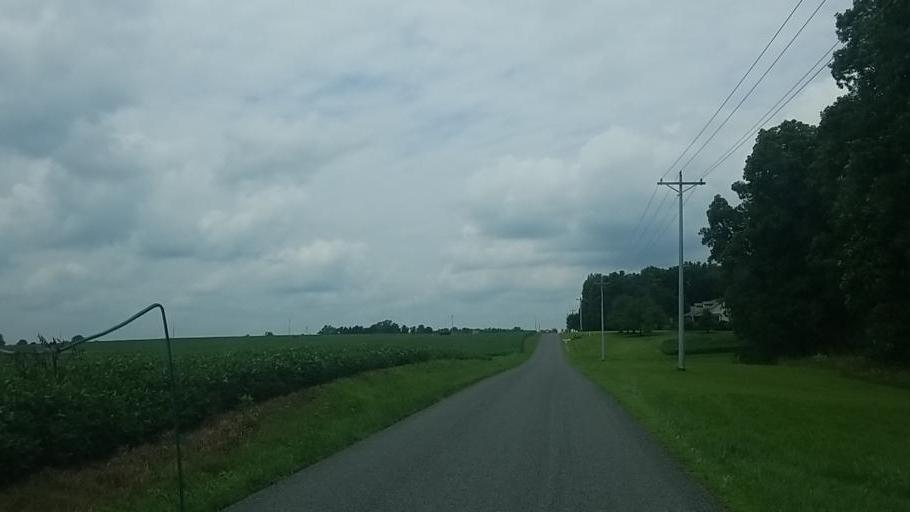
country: US
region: Ohio
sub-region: Licking County
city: Utica
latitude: 40.2385
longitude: -82.3915
